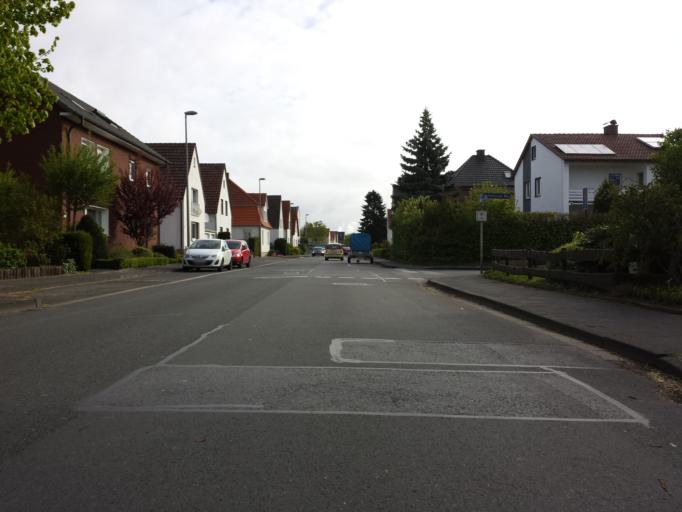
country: DE
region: North Rhine-Westphalia
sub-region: Regierungsbezirk Detmold
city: Guetersloh
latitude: 51.8921
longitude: 8.3591
